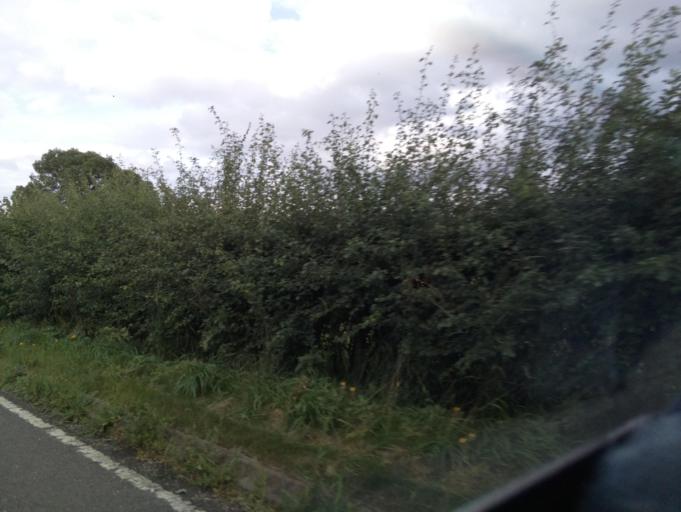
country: GB
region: England
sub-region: Warwickshire
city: Long Itchington
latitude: 52.2970
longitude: -1.3390
